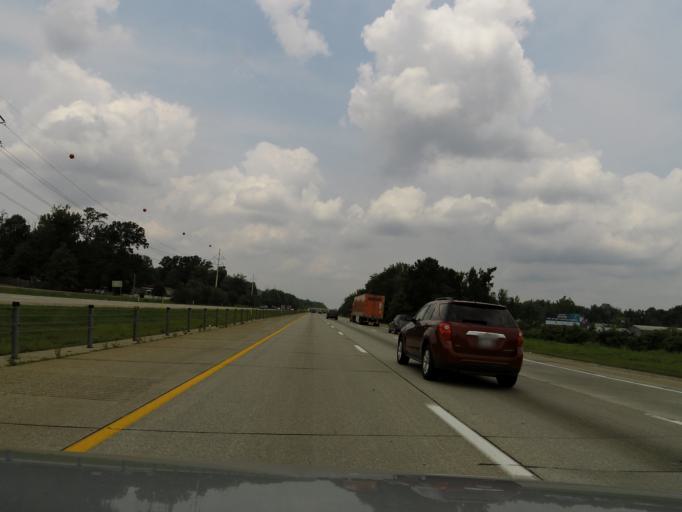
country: US
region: Kentucky
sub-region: Bullitt County
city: Hillview
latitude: 38.0823
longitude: -85.7006
